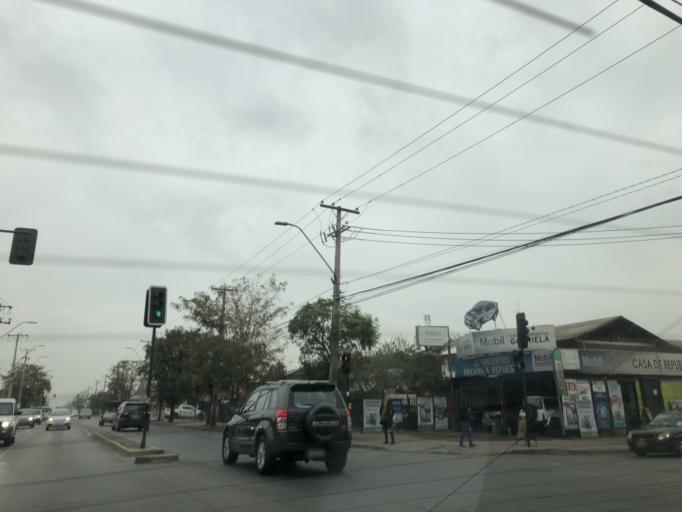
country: CL
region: Santiago Metropolitan
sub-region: Provincia de Santiago
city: La Pintana
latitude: -33.5821
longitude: -70.6028
